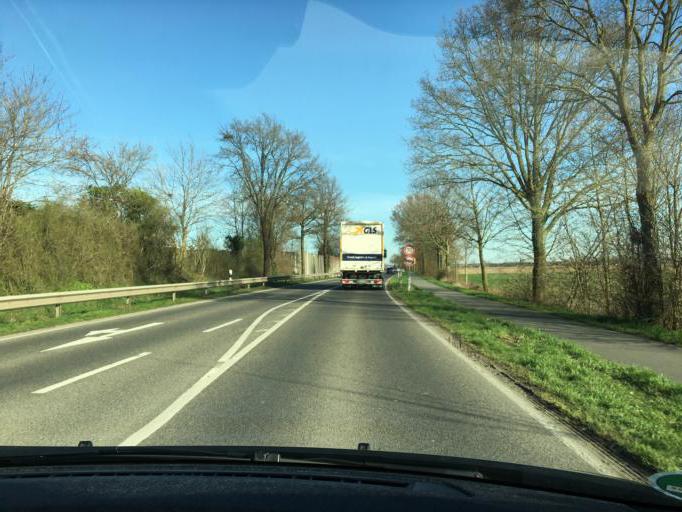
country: DE
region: North Rhine-Westphalia
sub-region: Regierungsbezirk Dusseldorf
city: Kaarst
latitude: 51.1935
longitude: 6.5997
